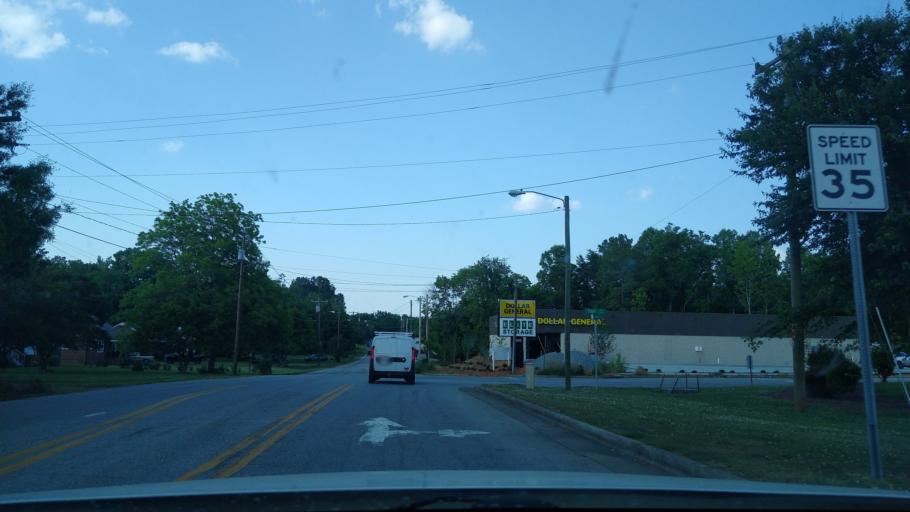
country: US
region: North Carolina
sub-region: Guilford County
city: Greensboro
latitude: 36.0284
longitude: -79.7698
